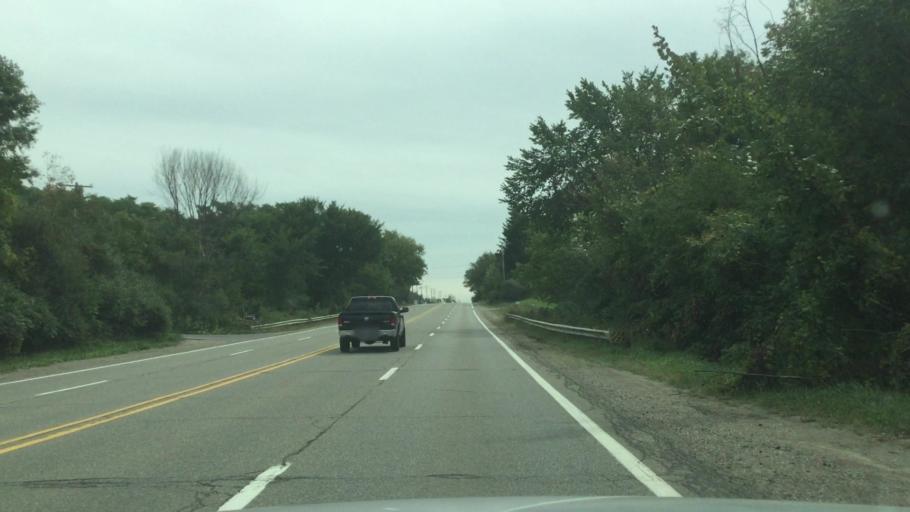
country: US
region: Michigan
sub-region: Oakland County
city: Ortonville
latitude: 42.7934
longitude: -83.5162
